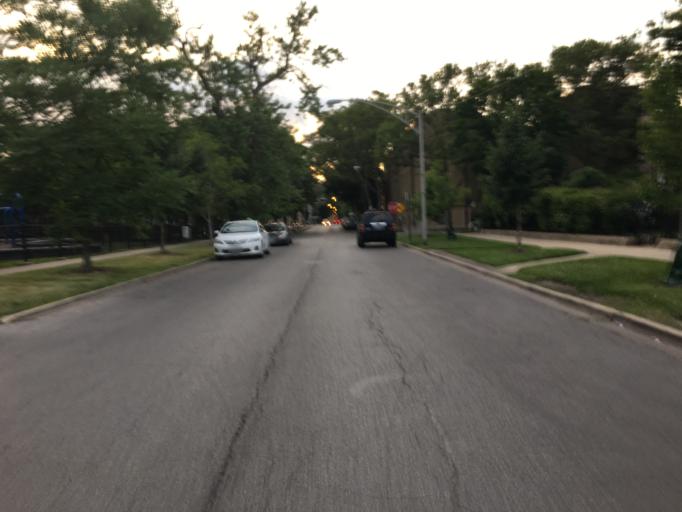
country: US
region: Illinois
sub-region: Cook County
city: Lincolnwood
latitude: 41.9653
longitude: -87.7001
